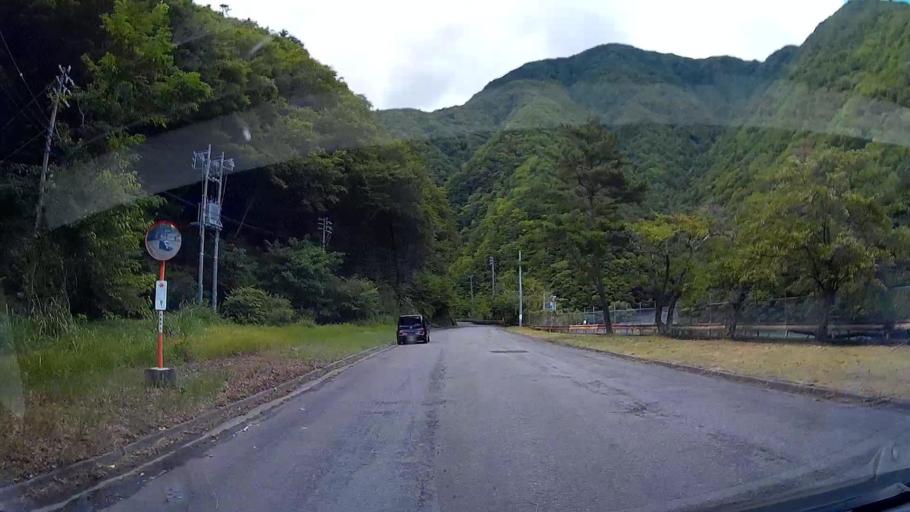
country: JP
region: Shizuoka
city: Shizuoka-shi
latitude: 35.3079
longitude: 138.2021
